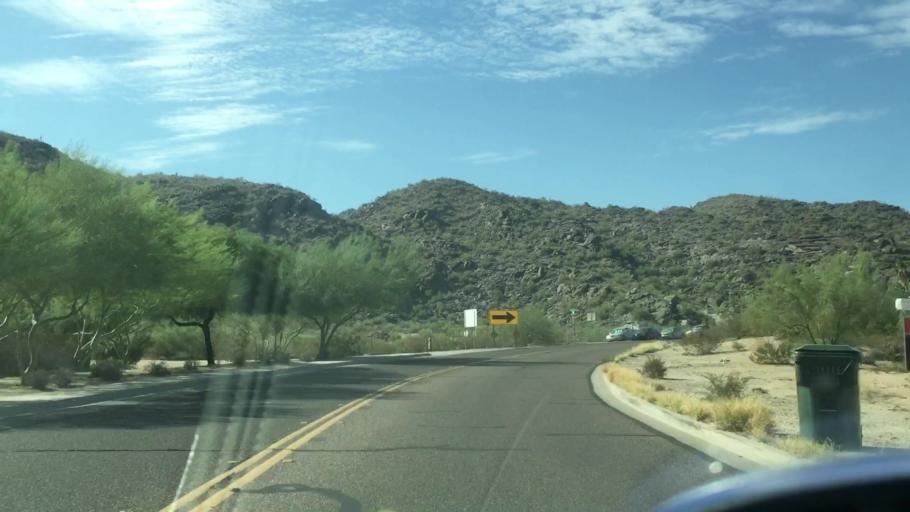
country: US
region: Arizona
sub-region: Maricopa County
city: Guadalupe
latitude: 33.3656
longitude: -112.0402
